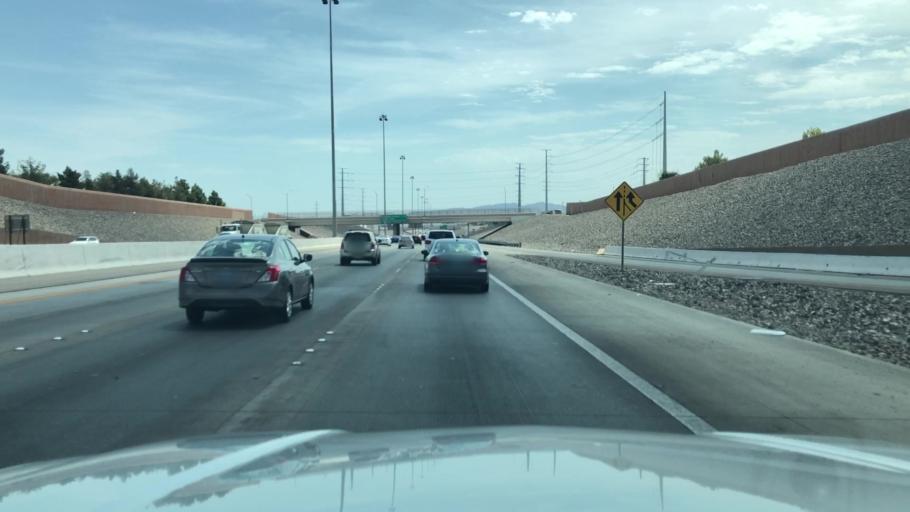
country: US
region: Nevada
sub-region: Clark County
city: Whitney
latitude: 36.0278
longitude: -115.0590
